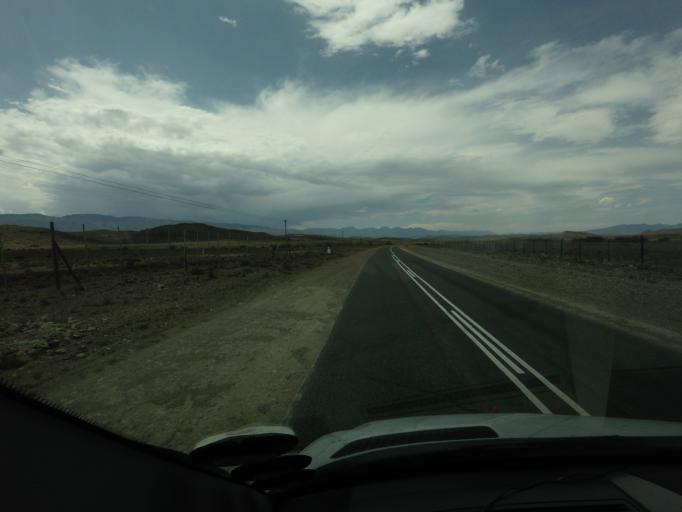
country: ZA
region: Western Cape
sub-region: Eden District Municipality
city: Ladismith
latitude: -33.6749
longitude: 20.9821
